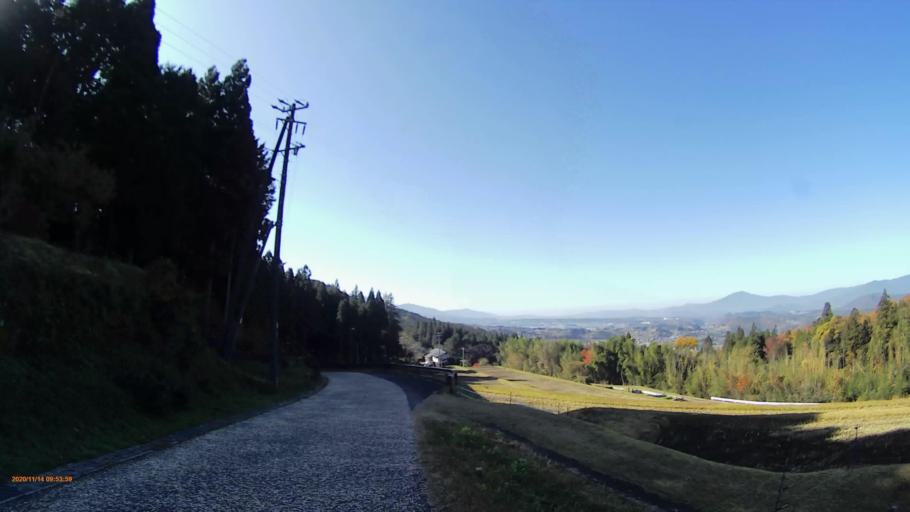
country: JP
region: Gifu
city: Nakatsugawa
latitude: 35.5170
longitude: 137.5521
